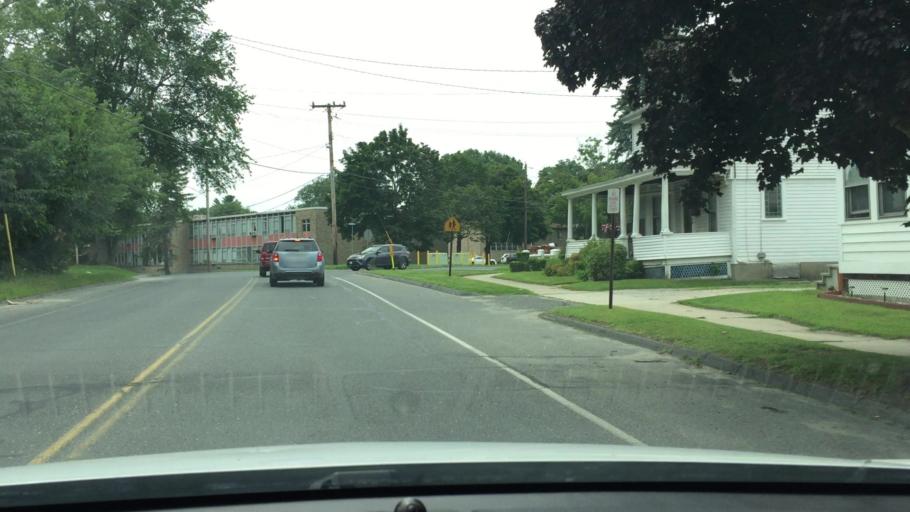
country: US
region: Massachusetts
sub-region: Berkshire County
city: Pittsfield
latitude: 42.4460
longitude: -73.2356
